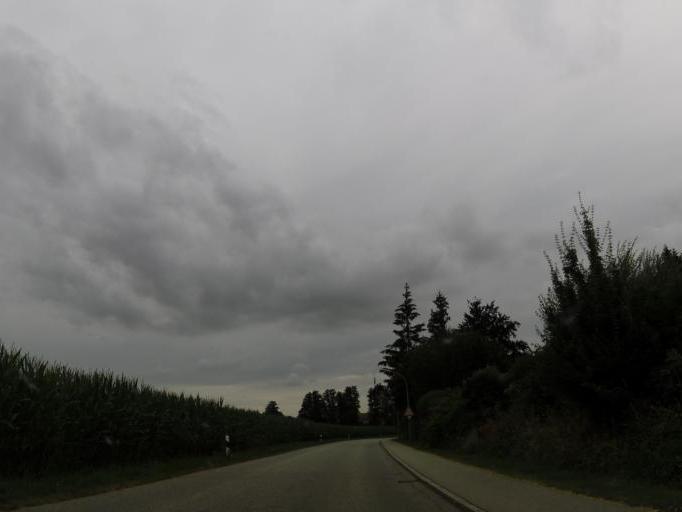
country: DE
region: Bavaria
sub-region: Upper Bavaria
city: Walpertskirchen
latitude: 48.2586
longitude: 11.9709
